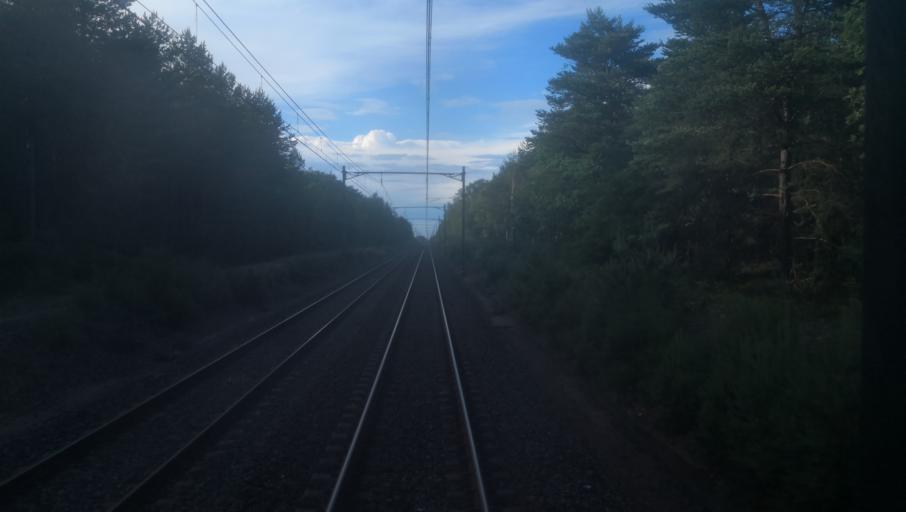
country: FR
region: Centre
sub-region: Departement du Loir-et-Cher
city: Theillay
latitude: 47.3536
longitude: 2.0475
